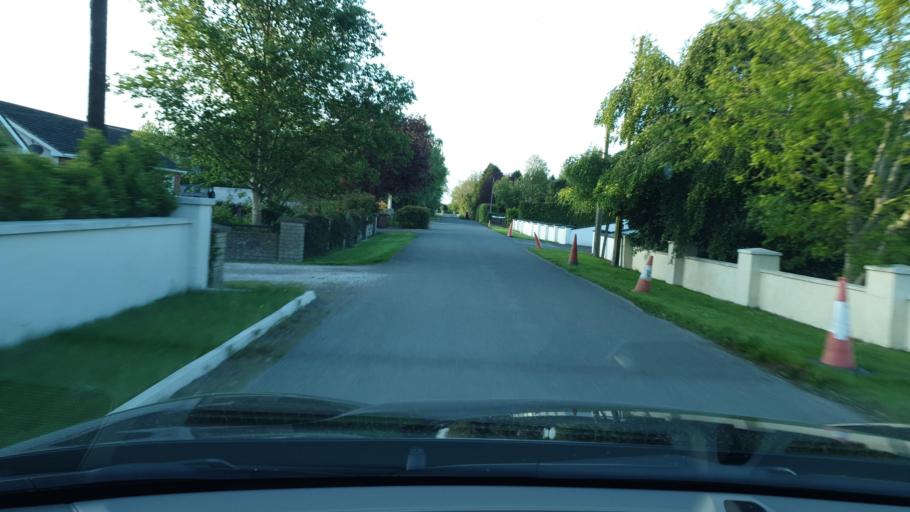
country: IE
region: Leinster
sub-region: An Mhi
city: Ashbourne
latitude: 53.4867
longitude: -6.4006
